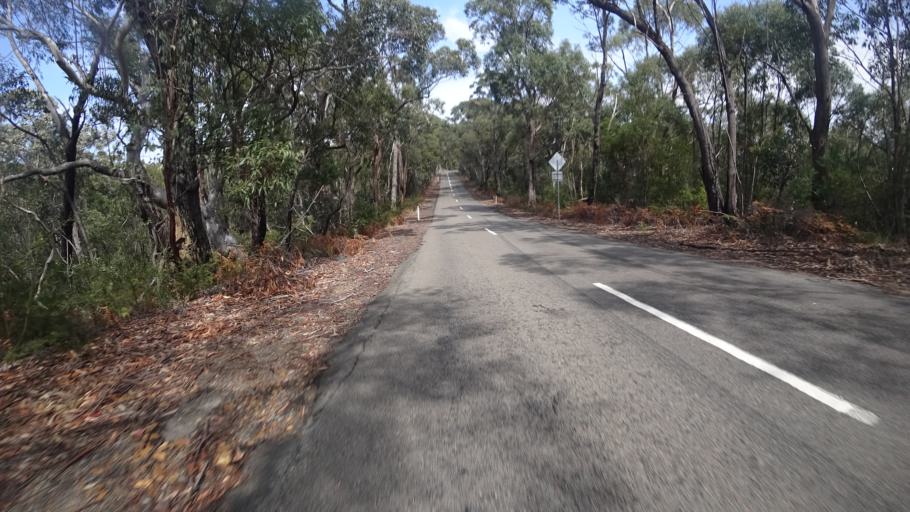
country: AU
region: New South Wales
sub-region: Hornsby Shire
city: Mount Colah
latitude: -33.6757
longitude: 151.1321
